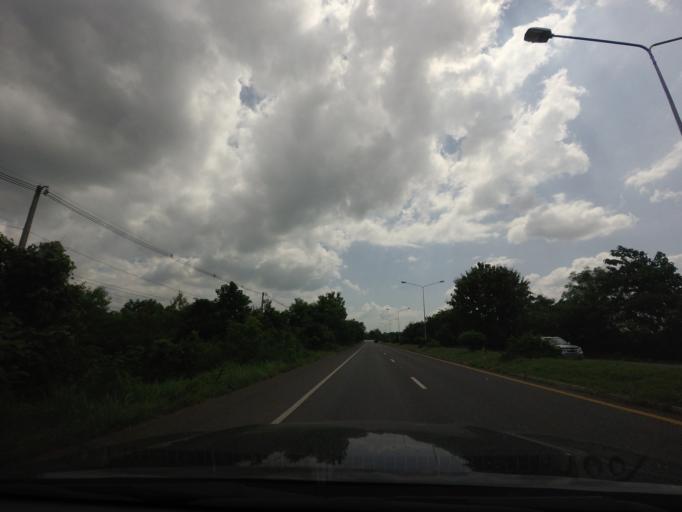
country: TH
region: Phetchabun
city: Nong Phai
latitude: 16.1872
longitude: 101.0889
